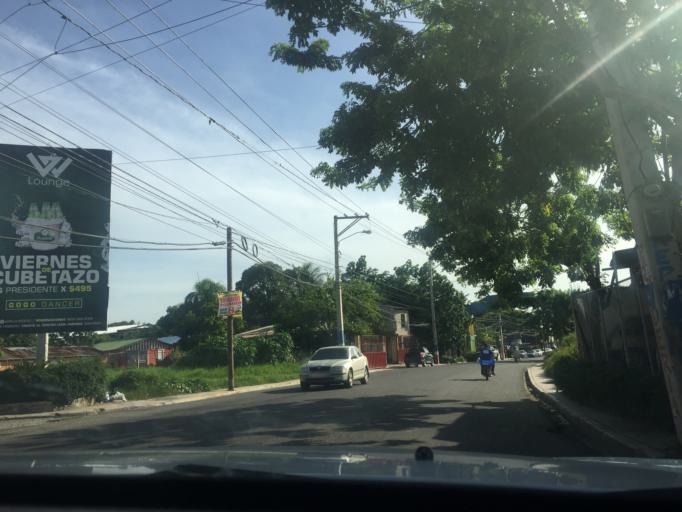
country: DO
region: Santiago
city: Tamboril
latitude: 19.4706
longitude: -70.6464
